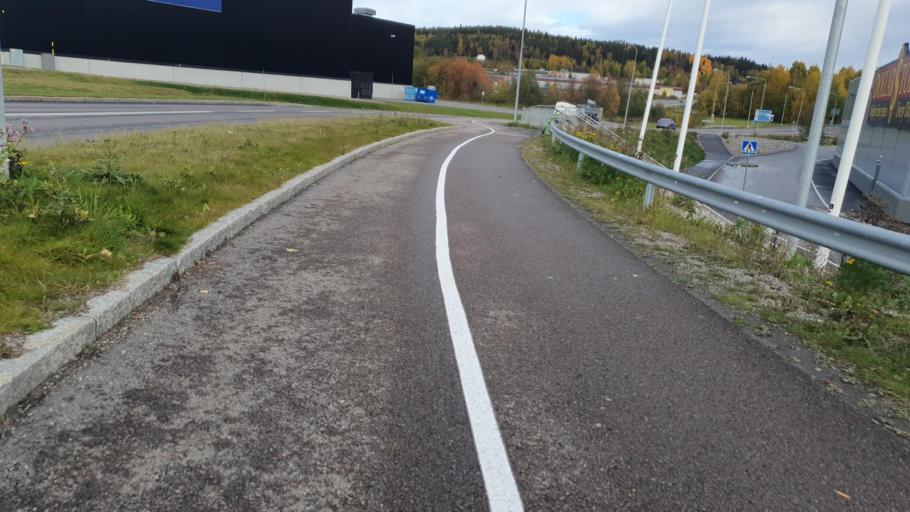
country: SE
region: Vaesternorrland
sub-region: Sundsvalls Kommun
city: Sundsbruk
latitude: 62.4439
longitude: 17.3417
